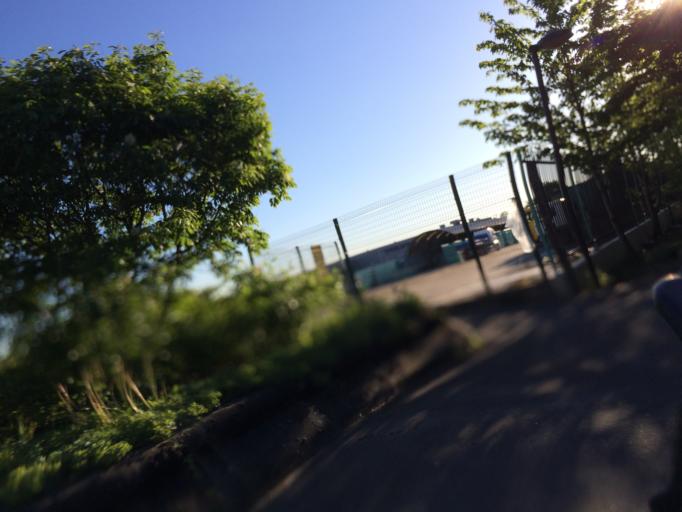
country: FR
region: Ile-de-France
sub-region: Departement de l'Essonne
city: Chilly-Mazarin
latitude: 48.7234
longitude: 2.3028
